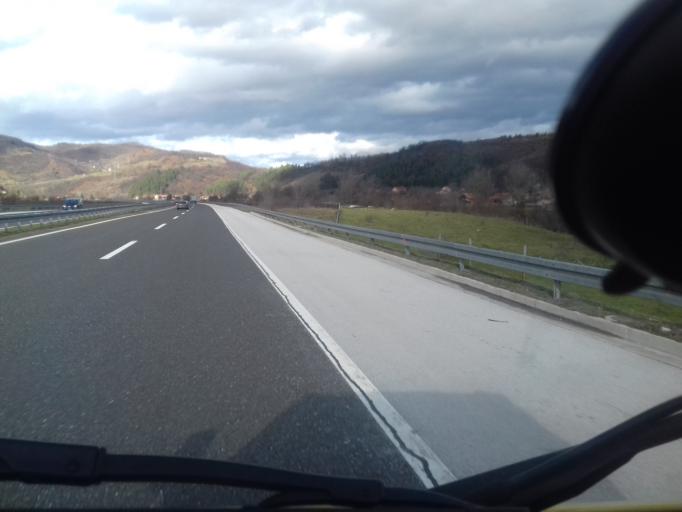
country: BA
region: Federation of Bosnia and Herzegovina
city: Mahala
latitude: 43.9864
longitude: 18.2287
